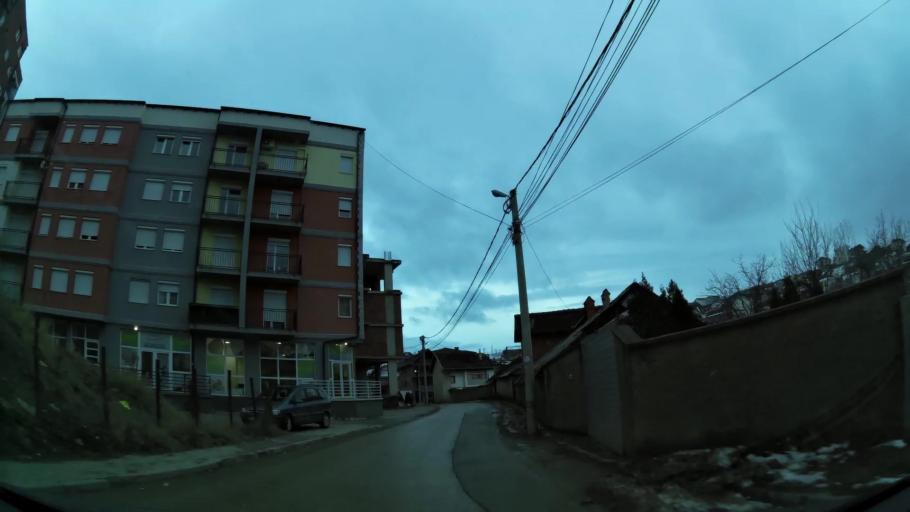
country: XK
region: Pristina
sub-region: Komuna e Prishtines
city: Pristina
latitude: 42.6428
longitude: 21.1678
